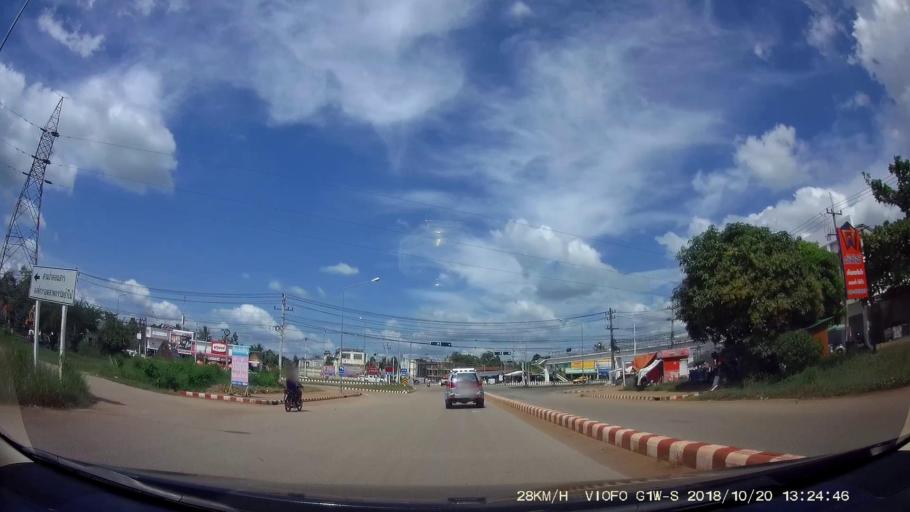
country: TH
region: Chaiyaphum
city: Khon San
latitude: 16.5945
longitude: 101.9269
